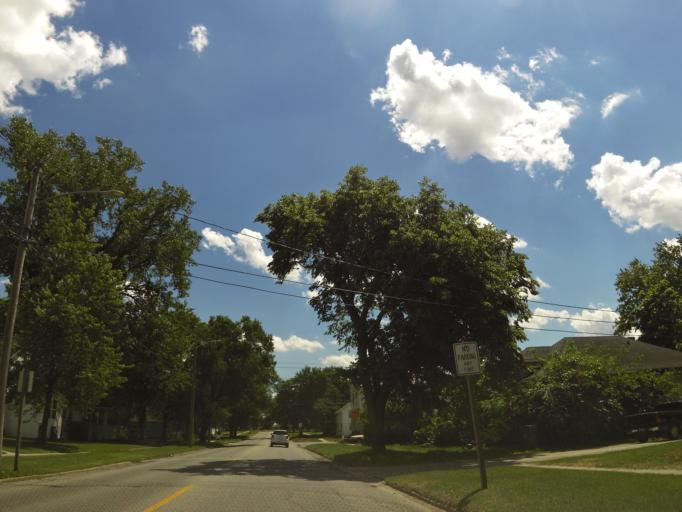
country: US
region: Iowa
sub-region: Buchanan County
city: Independence
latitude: 42.4754
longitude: -91.8894
